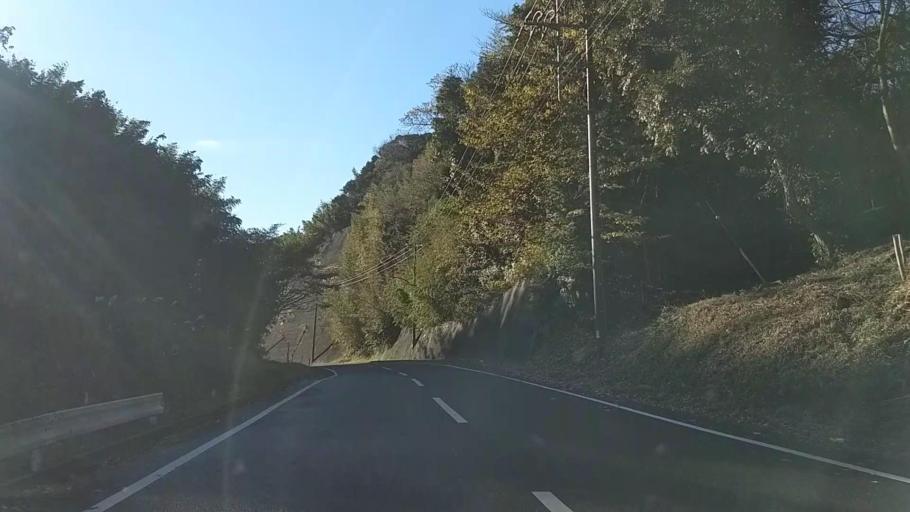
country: JP
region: Chiba
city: Futtsu
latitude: 35.2353
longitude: 139.8760
